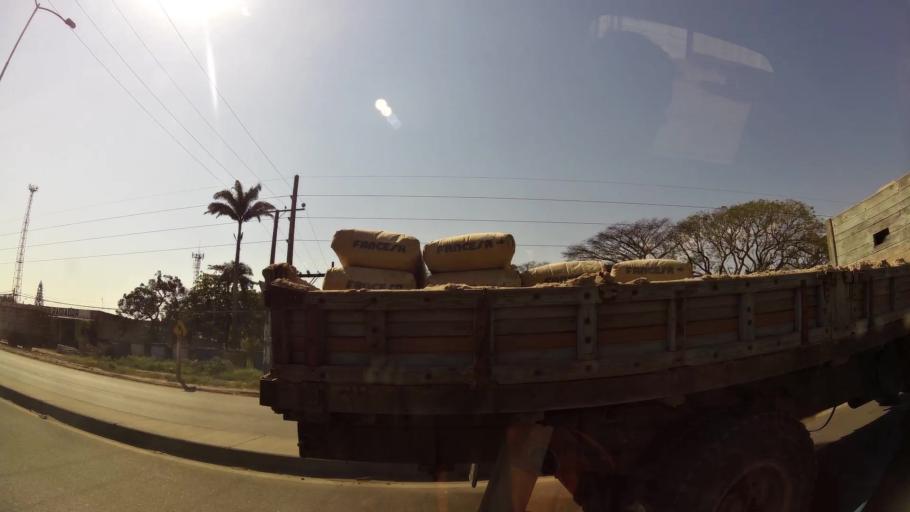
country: BO
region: Santa Cruz
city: Cotoca
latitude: -17.7643
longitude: -63.0976
